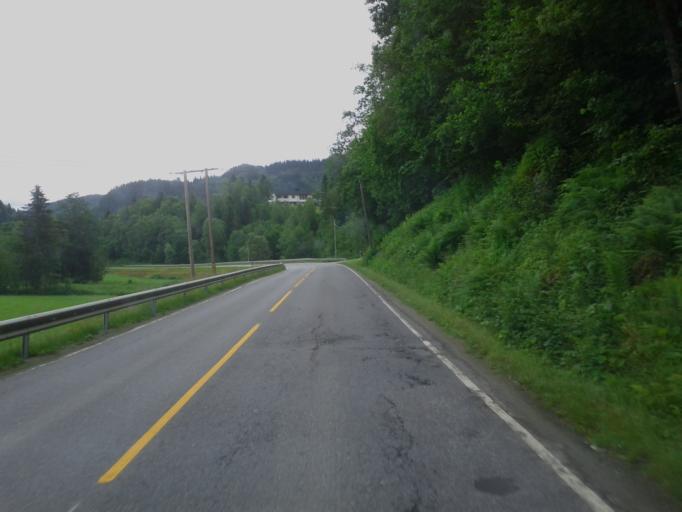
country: NO
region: Sor-Trondelag
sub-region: Midtre Gauldal
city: Storen
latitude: 63.0012
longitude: 10.4582
